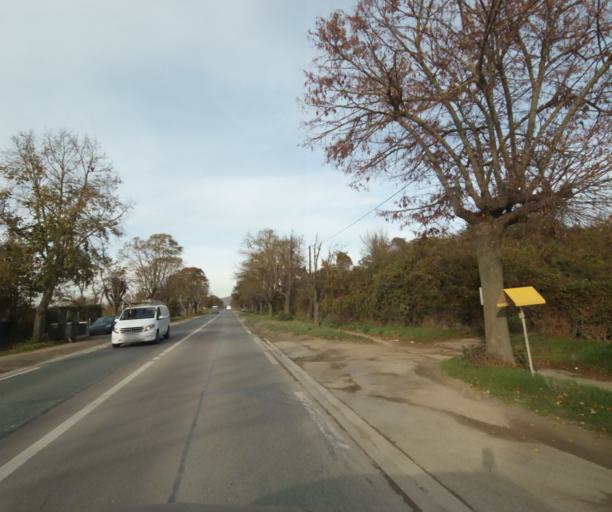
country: FR
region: Ile-de-France
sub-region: Departement des Yvelines
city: Triel-sur-Seine
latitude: 48.9586
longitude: 2.0178
